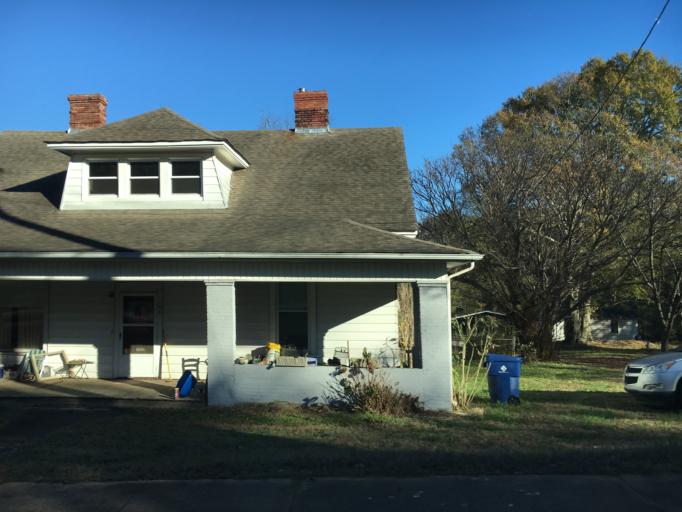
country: US
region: South Carolina
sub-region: Spartanburg County
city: Duncan
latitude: 34.9369
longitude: -82.1451
